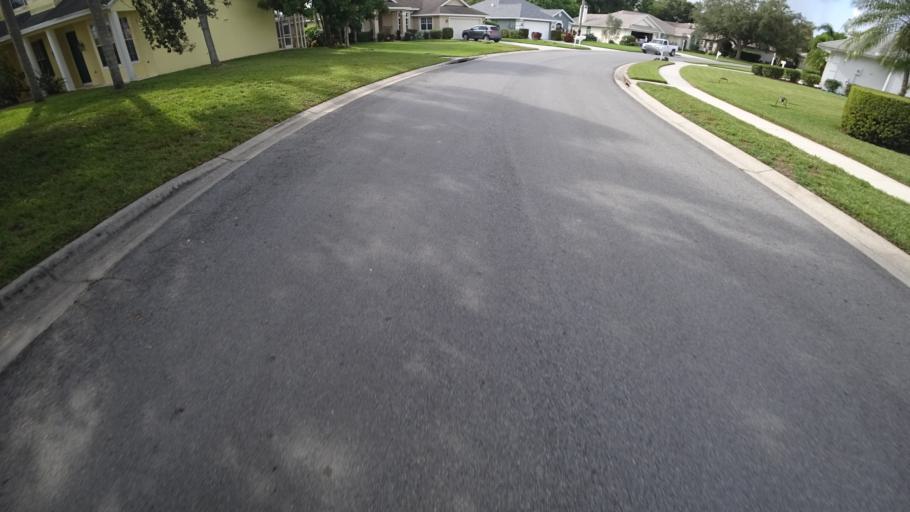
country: US
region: Florida
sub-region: Sarasota County
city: Desoto Lakes
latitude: 27.4182
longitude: -82.4853
